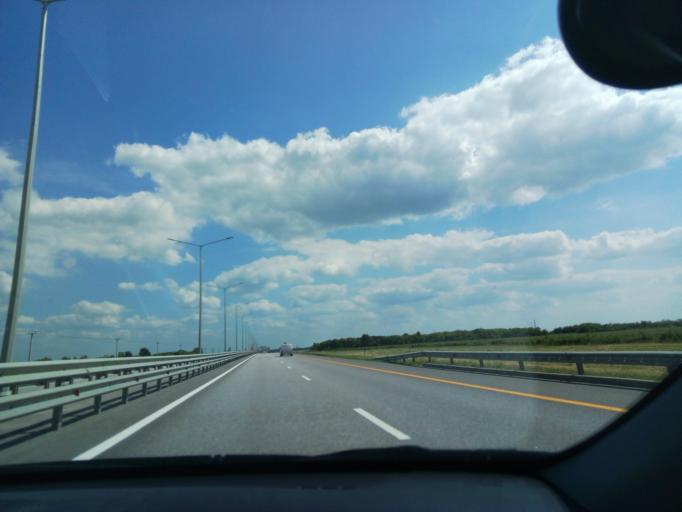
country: RU
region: Voronezj
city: Podkletnoye
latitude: 51.5019
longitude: 39.5206
